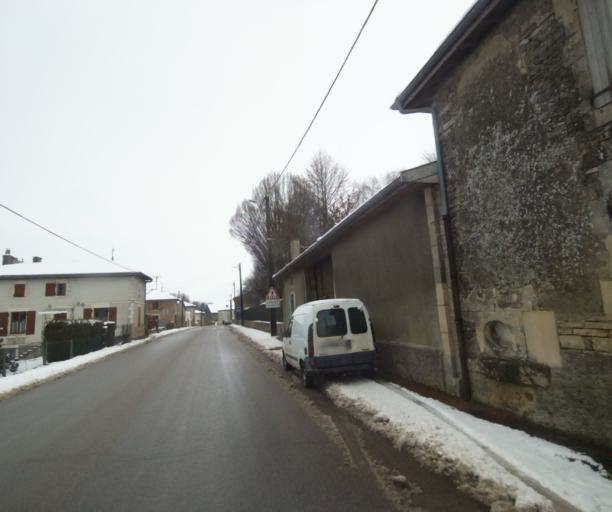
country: FR
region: Champagne-Ardenne
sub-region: Departement de la Haute-Marne
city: Wassy
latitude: 48.4555
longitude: 4.9630
